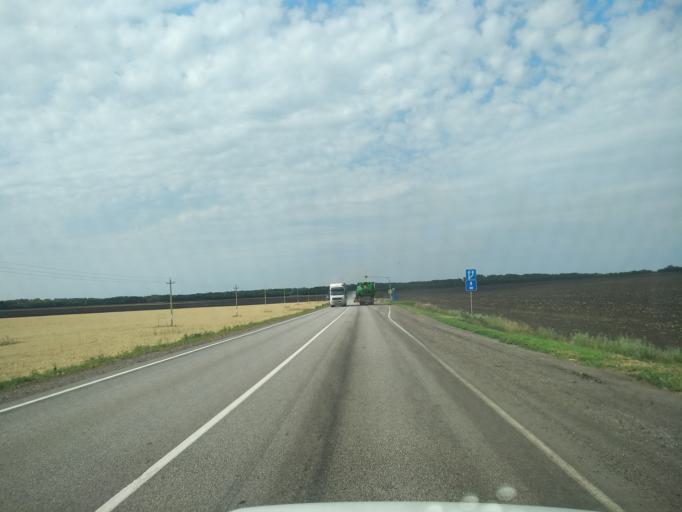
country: RU
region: Lipetsk
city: Dobrinka
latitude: 51.8855
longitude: 40.4282
